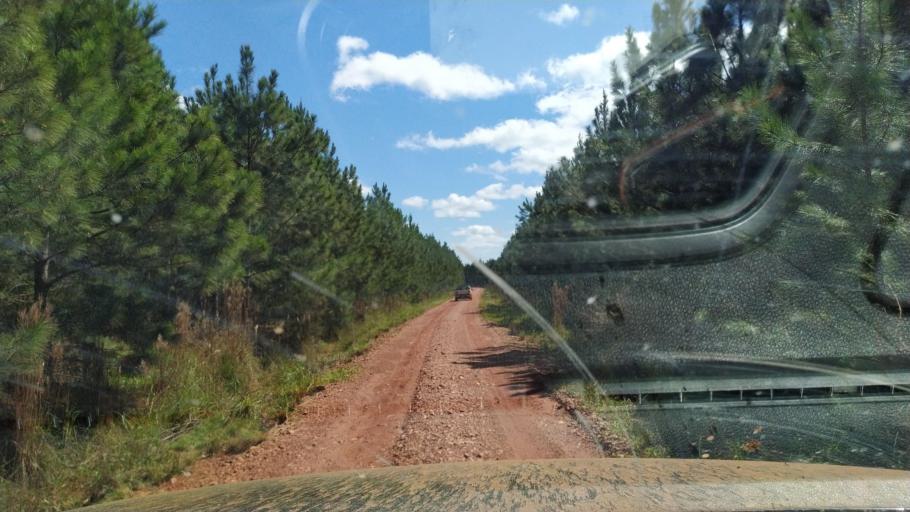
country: AR
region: Corrientes
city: Santo Tome
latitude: -28.4623
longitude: -55.9832
